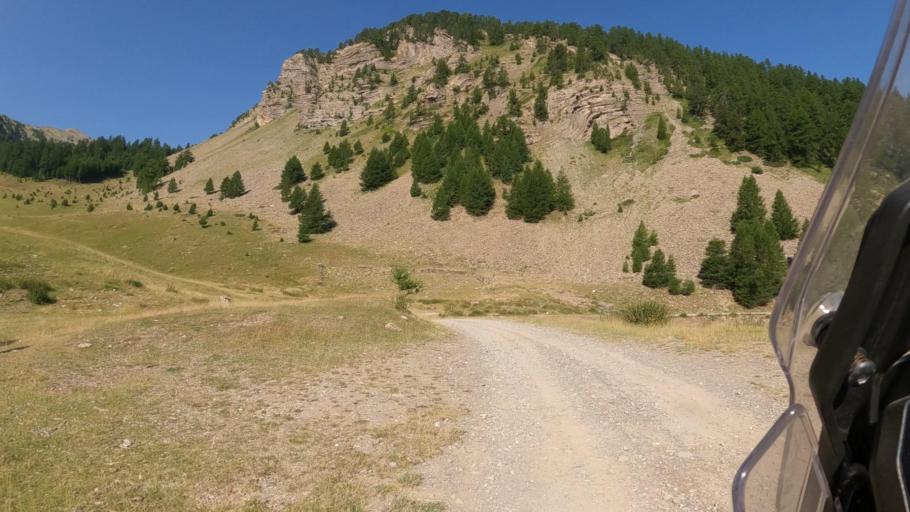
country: FR
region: Provence-Alpes-Cote d'Azur
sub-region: Departement des Hautes-Alpes
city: Guillestre
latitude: 44.5843
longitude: 6.5979
